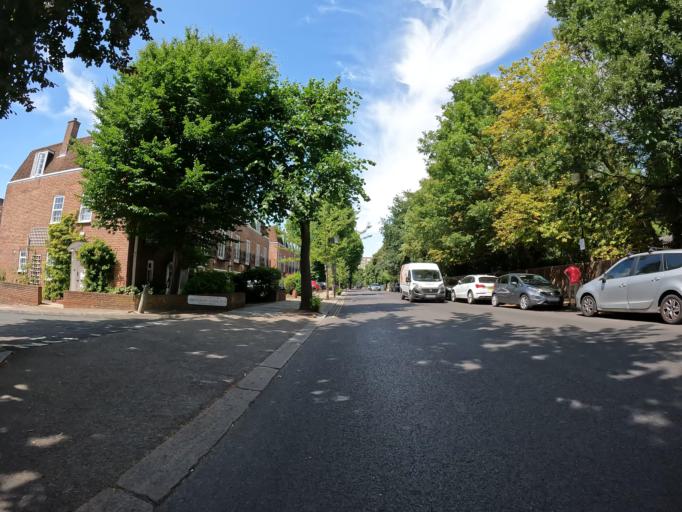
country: GB
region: England
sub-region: Greater London
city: Kensington
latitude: 51.5019
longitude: -0.2066
